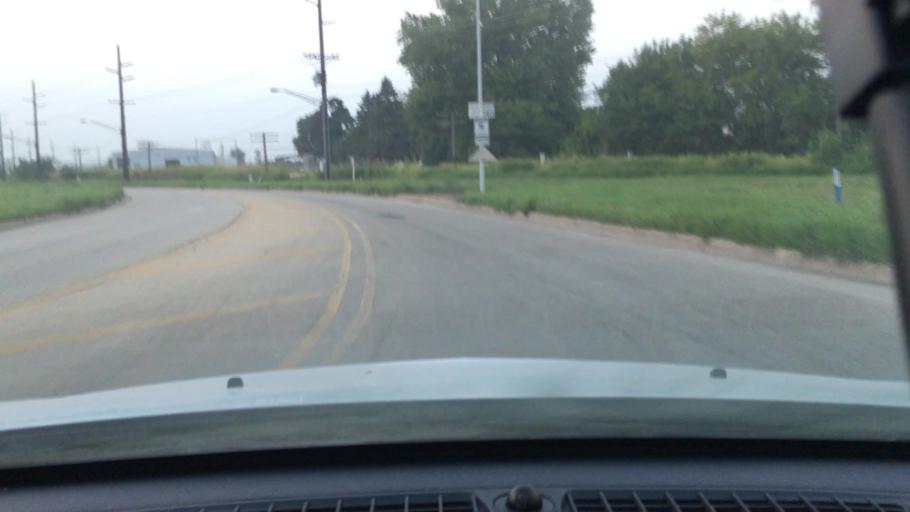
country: US
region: Illinois
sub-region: Ogle County
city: Rochelle
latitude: 41.9195
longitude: -89.0547
